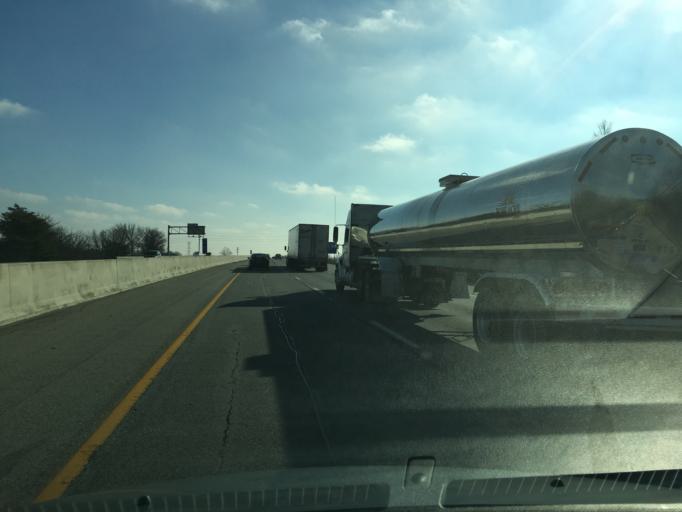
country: US
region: Indiana
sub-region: Marion County
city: Speedway
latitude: 39.8557
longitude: -86.2670
